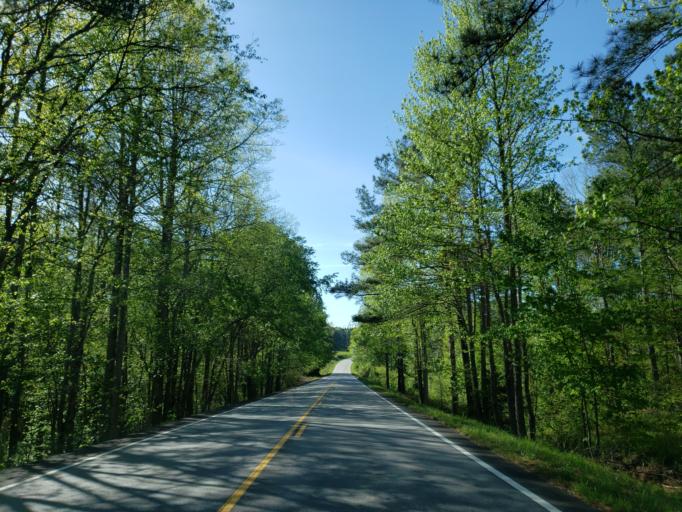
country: US
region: Georgia
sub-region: Haralson County
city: Tallapoosa
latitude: 33.8771
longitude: -85.3057
